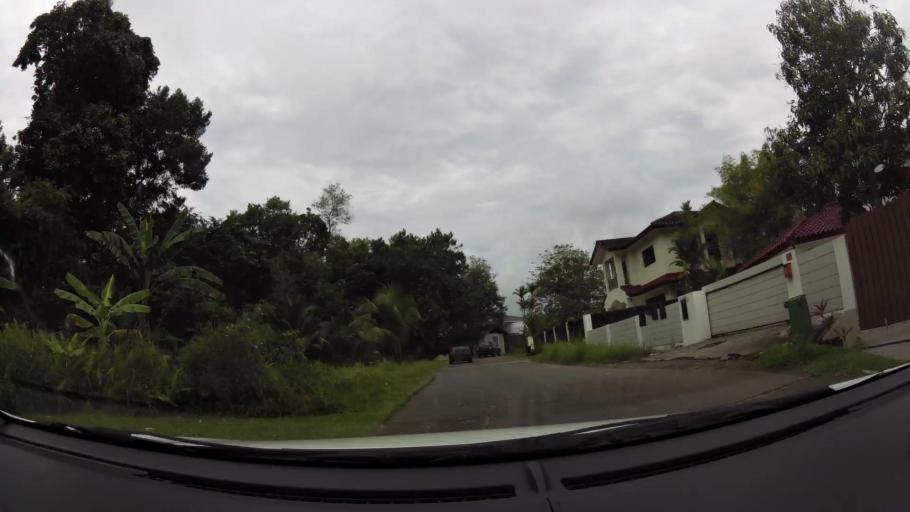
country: BN
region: Brunei and Muara
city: Bandar Seri Begawan
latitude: 4.8870
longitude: 114.9249
